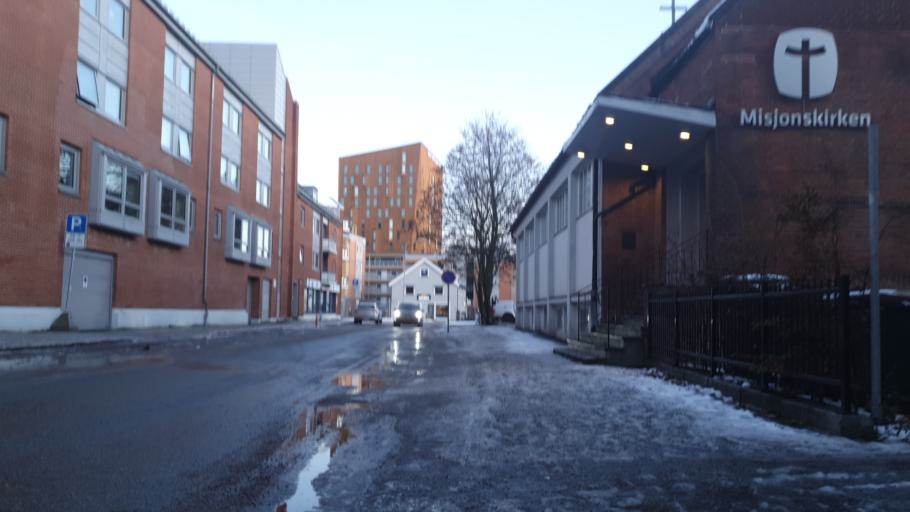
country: NO
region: Buskerud
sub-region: Drammen
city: Drammen
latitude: 59.7375
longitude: 10.2051
